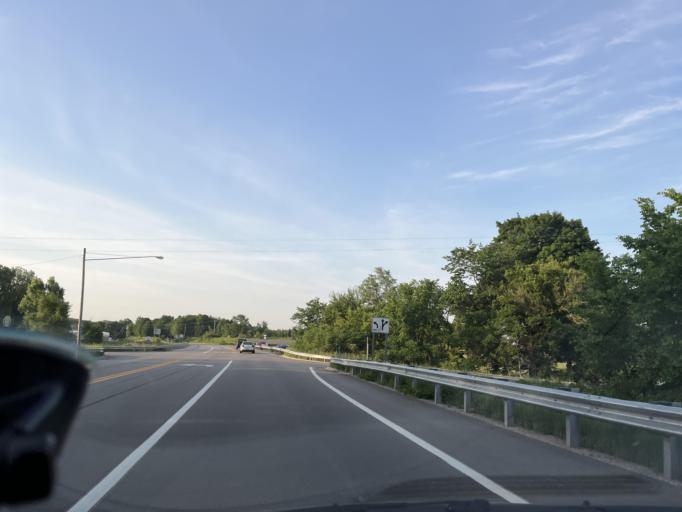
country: US
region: Michigan
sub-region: Kent County
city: Caledonia
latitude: 42.7548
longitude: -85.5054
